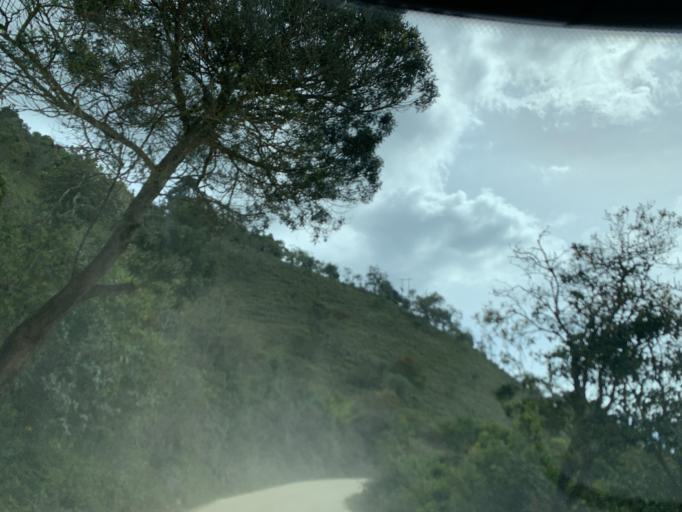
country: CO
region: Santander
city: Capitanejo
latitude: 6.5038
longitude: -72.7345
